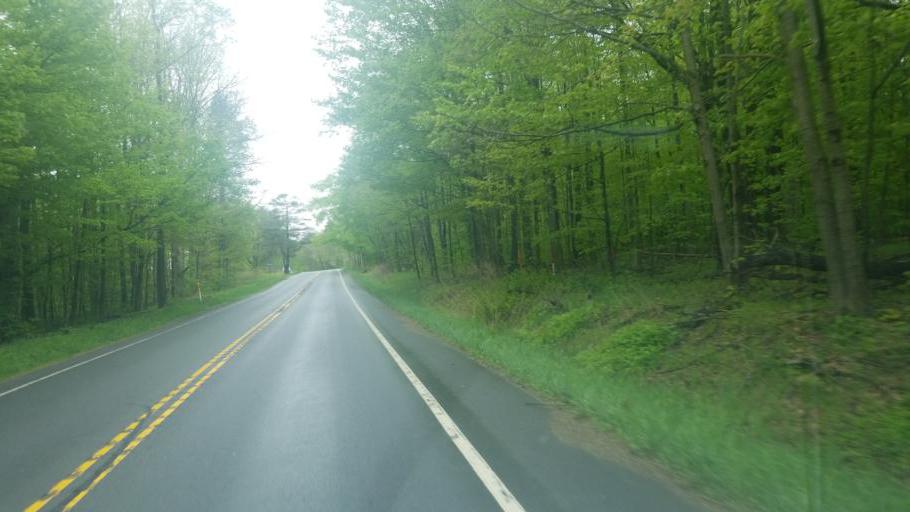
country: US
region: Pennsylvania
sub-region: McKean County
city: Kane
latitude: 41.5824
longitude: -78.8590
